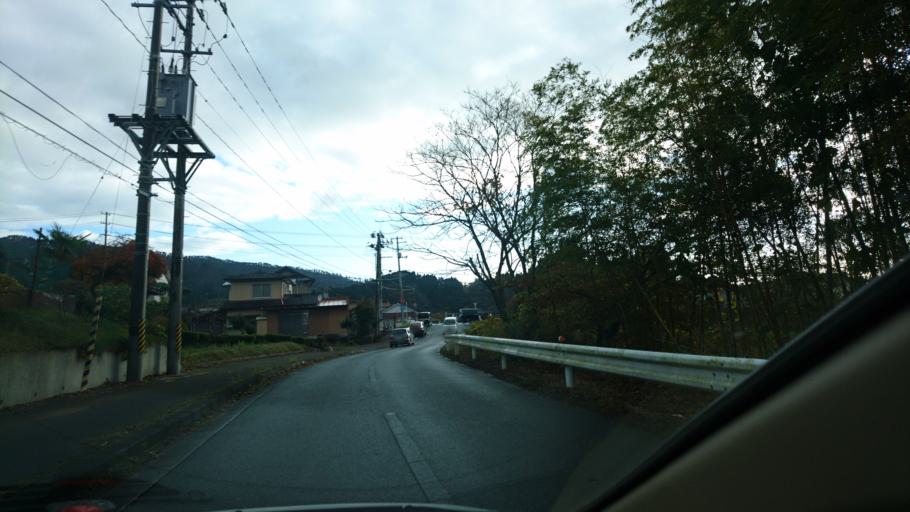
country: JP
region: Iwate
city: Ofunato
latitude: 38.9103
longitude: 141.5436
